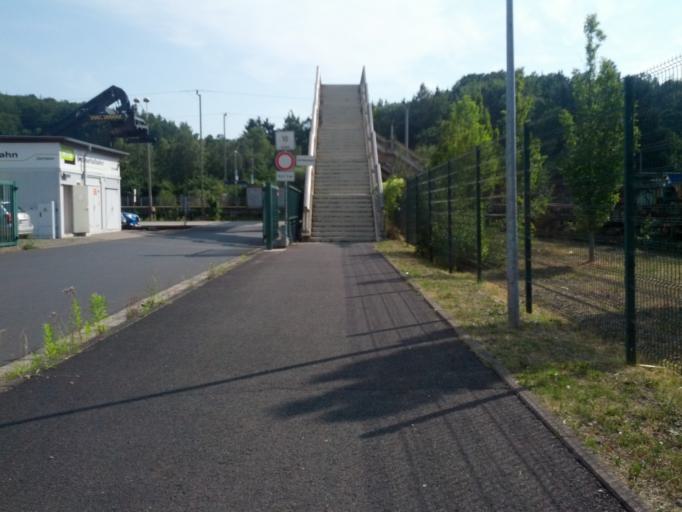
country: DE
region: Thuringia
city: Eisenach
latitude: 50.9800
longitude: 10.2838
